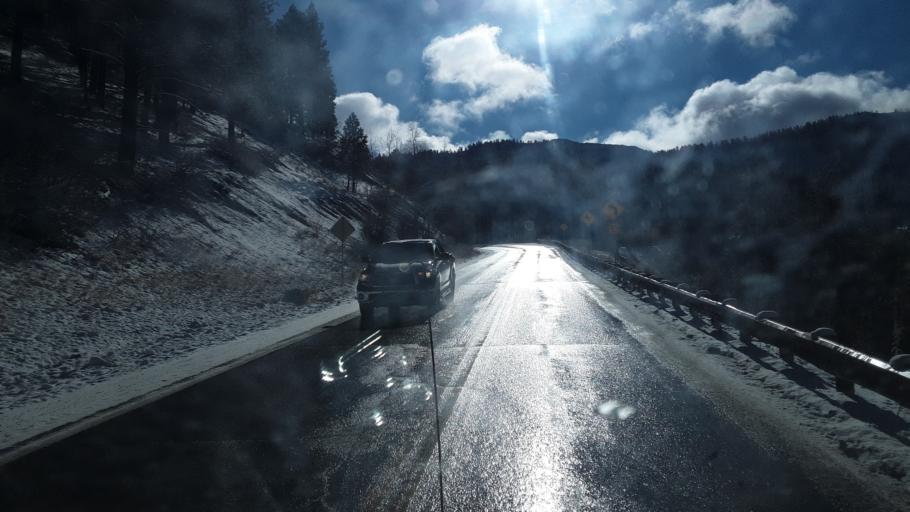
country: US
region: Colorado
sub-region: La Plata County
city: Durango
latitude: 37.3317
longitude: -107.7375
